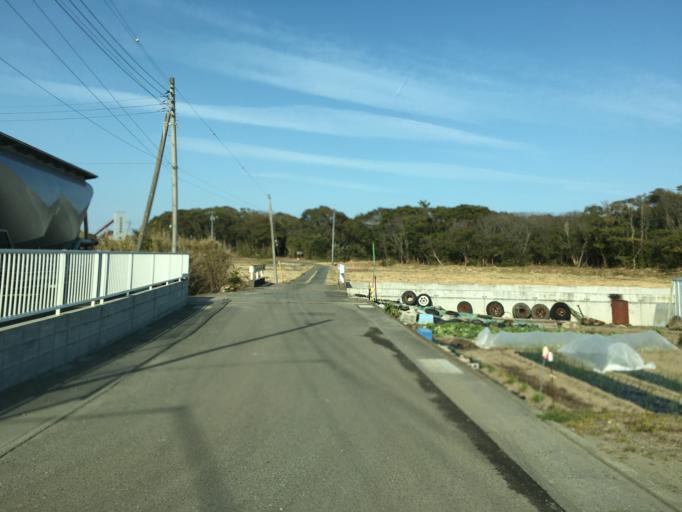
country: JP
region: Ibaraki
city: Takahagi
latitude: 36.7428
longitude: 140.7291
